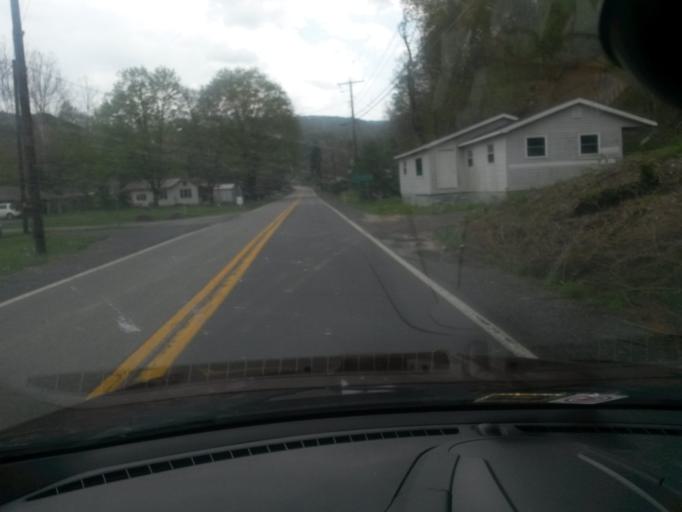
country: US
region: West Virginia
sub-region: Greenbrier County
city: White Sulphur Springs
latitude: 37.7988
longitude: -80.2797
